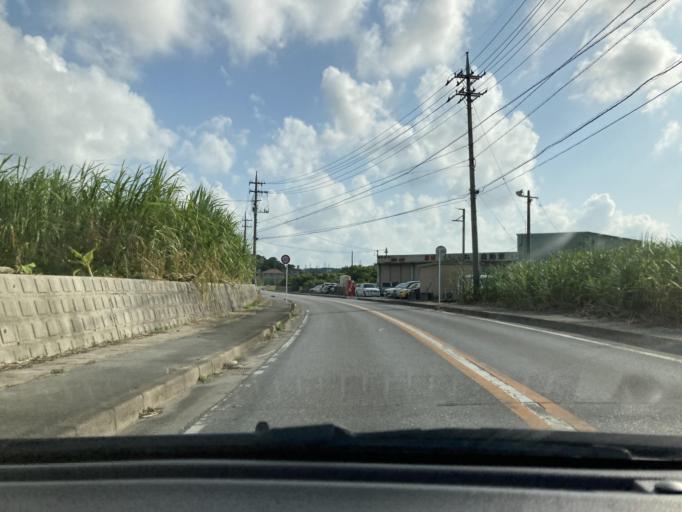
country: JP
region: Okinawa
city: Itoman
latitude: 26.1409
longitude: 127.7009
